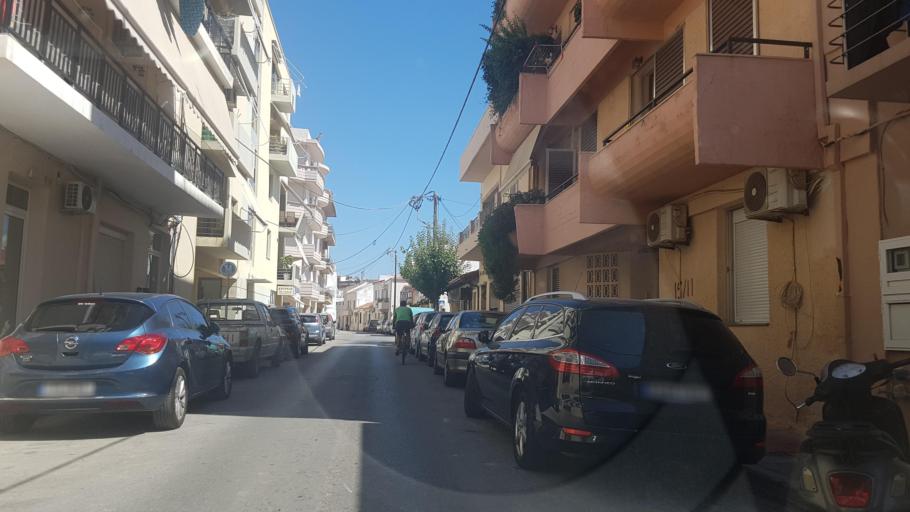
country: GR
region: Crete
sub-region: Nomos Chanias
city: Chania
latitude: 35.5146
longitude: 24.0098
